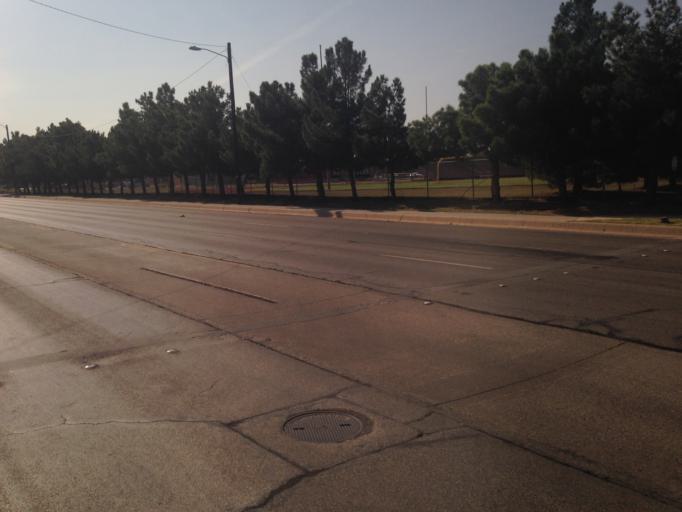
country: US
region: Texas
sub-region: Midland County
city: Midland
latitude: 32.0189
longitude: -102.1290
